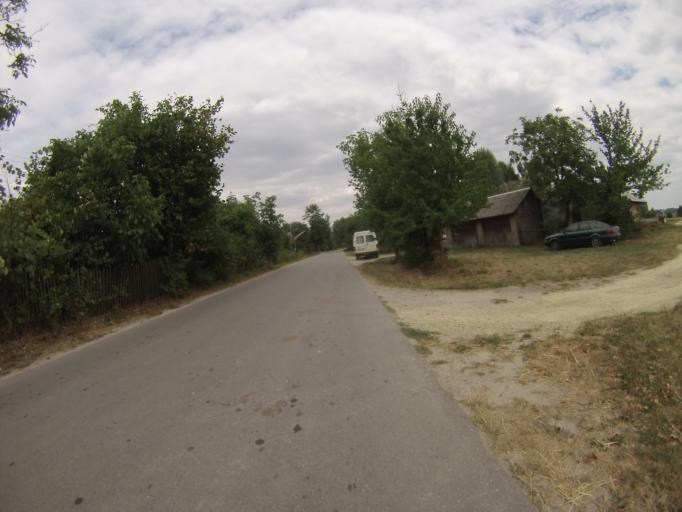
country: PL
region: Swietokrzyskie
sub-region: Powiat staszowski
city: Bogoria
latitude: 50.6849
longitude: 21.2009
